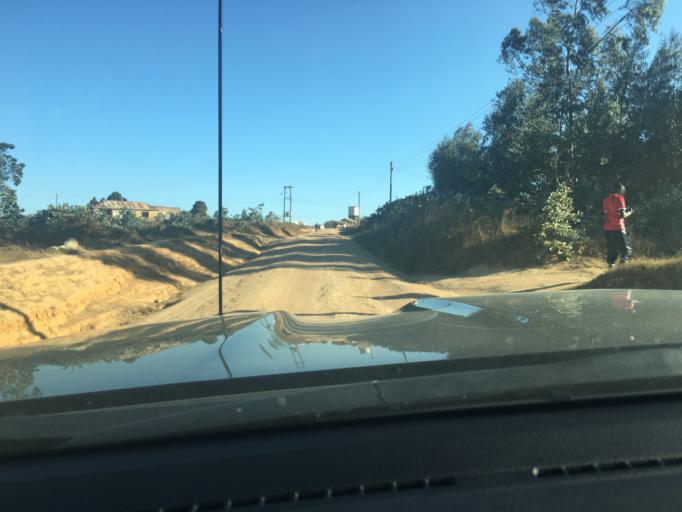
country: TZ
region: Iringa
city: Makungu
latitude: -8.4166
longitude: 35.4203
